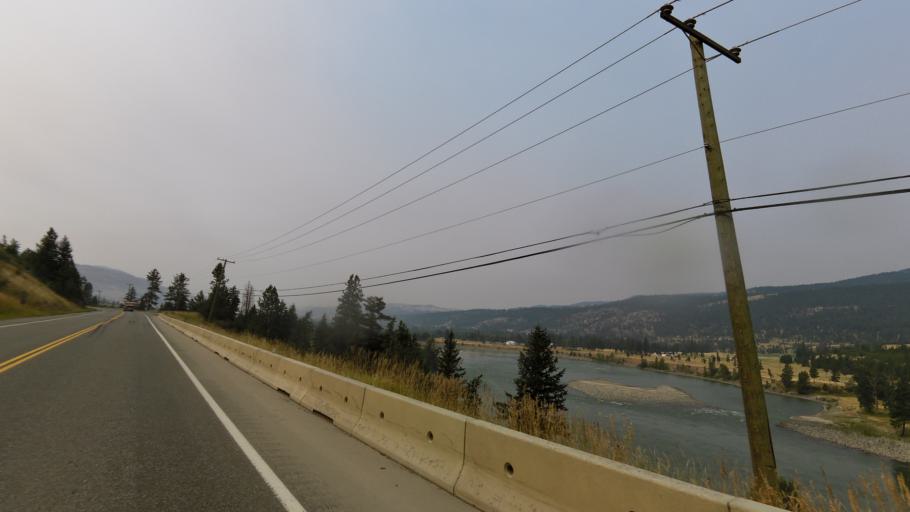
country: CA
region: British Columbia
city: Kamloops
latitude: 50.8760
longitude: -120.2622
